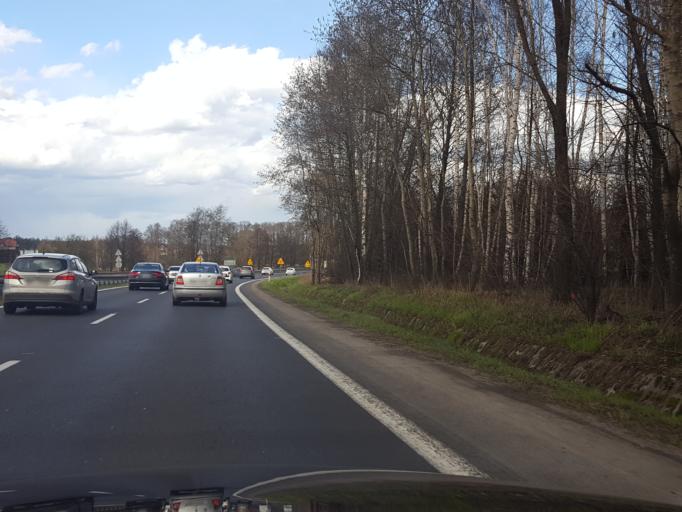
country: PL
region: Silesian Voivodeship
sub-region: Powiat pszczynski
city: Piasek
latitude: 50.0042
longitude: 18.9519
